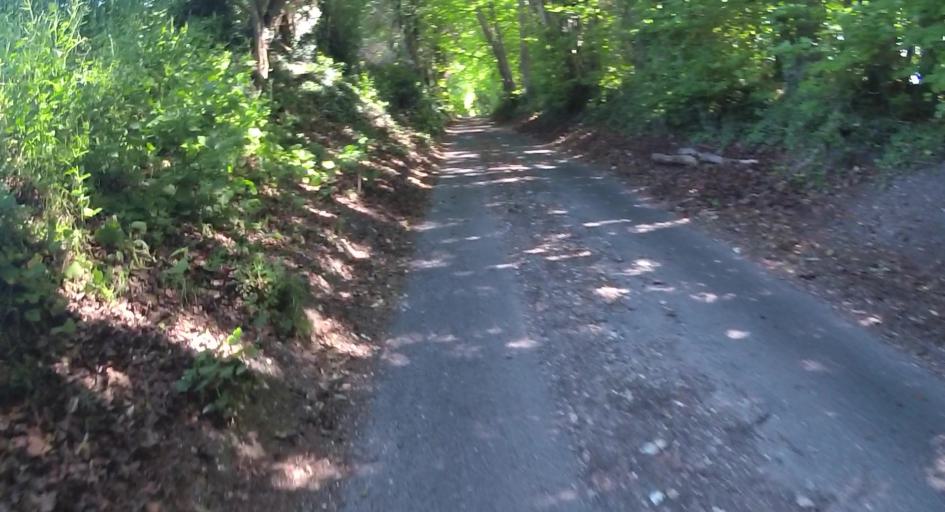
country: GB
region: England
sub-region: Hampshire
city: Old Basing
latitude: 51.2285
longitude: -1.0258
